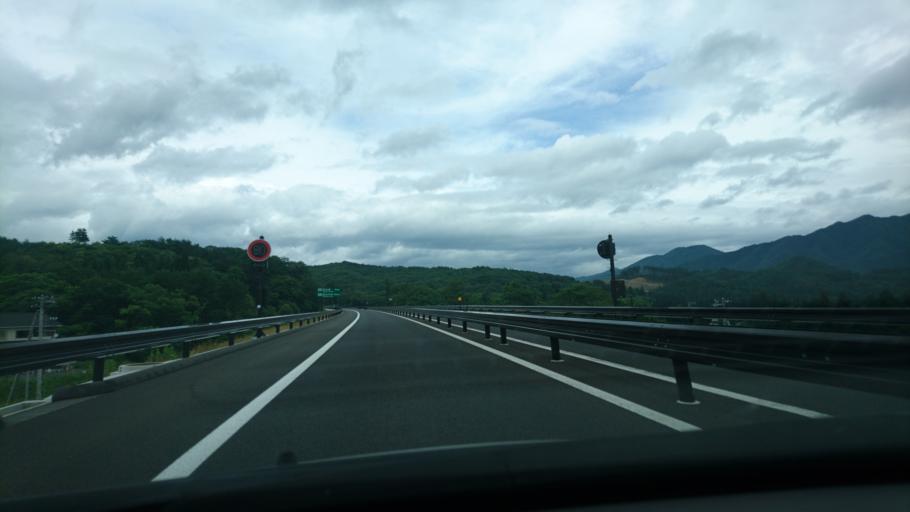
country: JP
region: Iwate
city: Yamada
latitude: 39.5431
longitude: 141.9226
